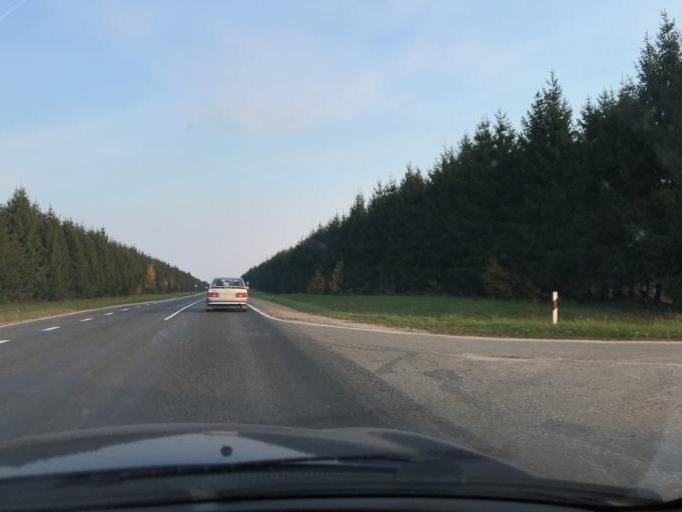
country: BY
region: Grodnenskaya
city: Karelichy
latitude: 53.5921
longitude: 26.0833
